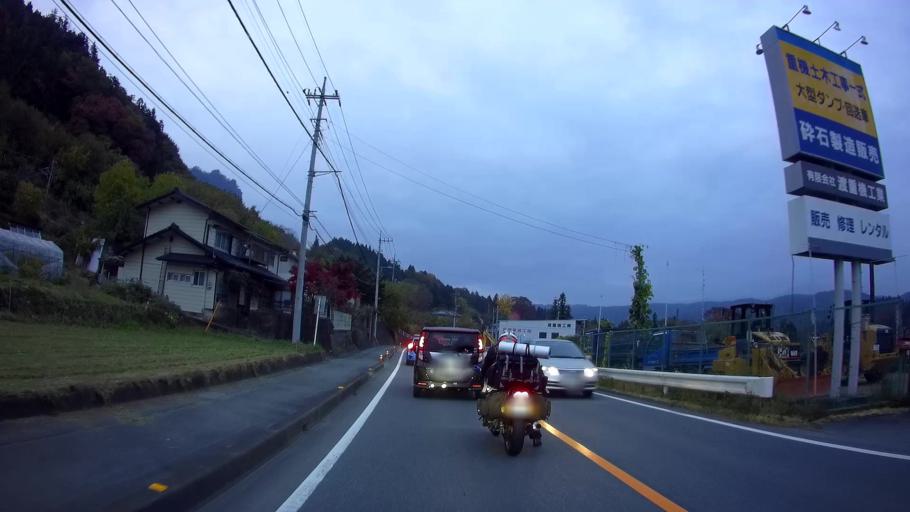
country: JP
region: Gunma
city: Nakanojomachi
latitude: 36.5536
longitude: 138.7802
